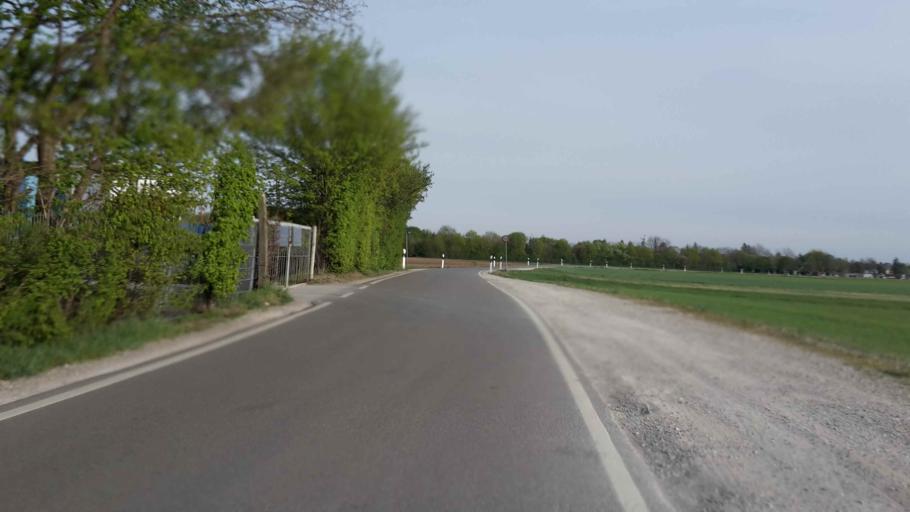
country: DE
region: Bavaria
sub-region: Upper Bavaria
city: Pasing
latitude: 48.1796
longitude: 11.4521
